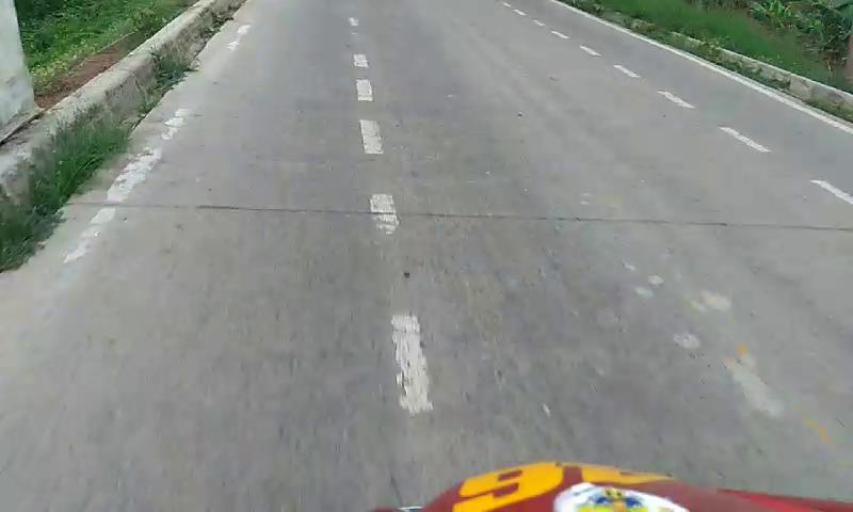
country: ID
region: West Java
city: Bekasi
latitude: -6.1443
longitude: 106.9702
